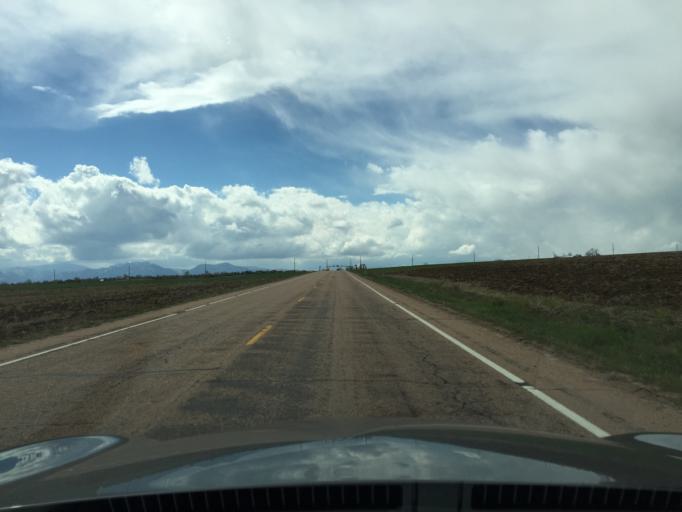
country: US
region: Colorado
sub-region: Boulder County
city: Lafayette
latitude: 40.0148
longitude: -105.0684
